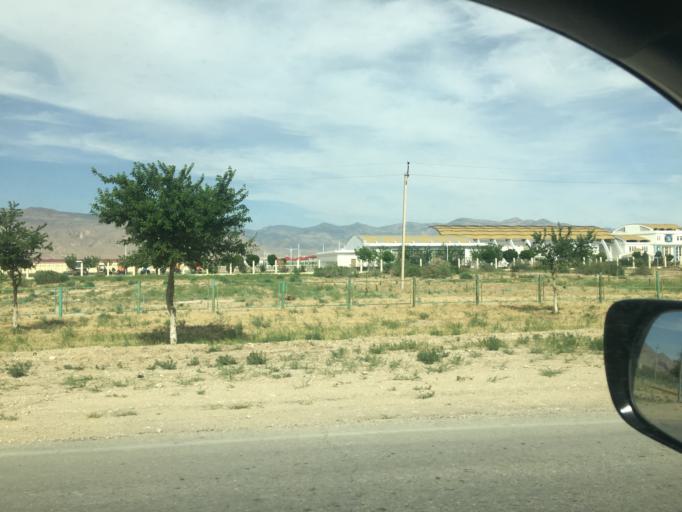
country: TM
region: Balkan
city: Balkanabat
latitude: 39.5749
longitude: 54.2695
